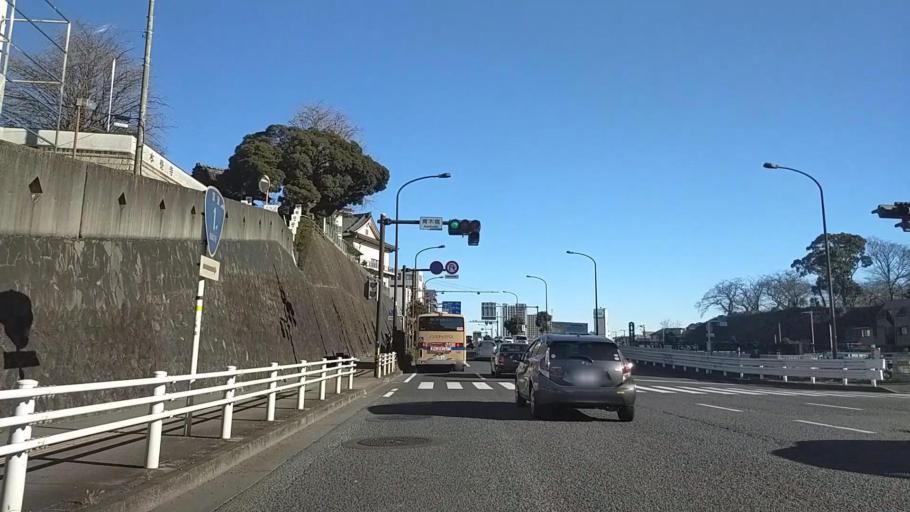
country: JP
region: Kanagawa
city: Yokohama
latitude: 35.4710
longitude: 139.6264
